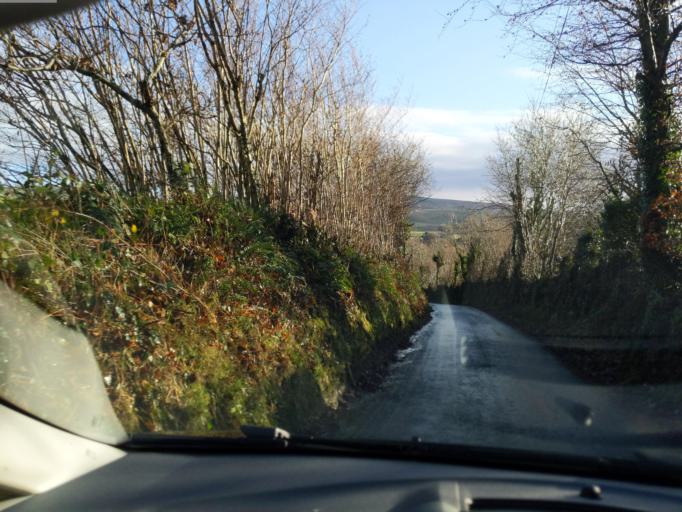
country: GB
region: England
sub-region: Devon
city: Okehampton
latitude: 50.7162
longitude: -4.0492
